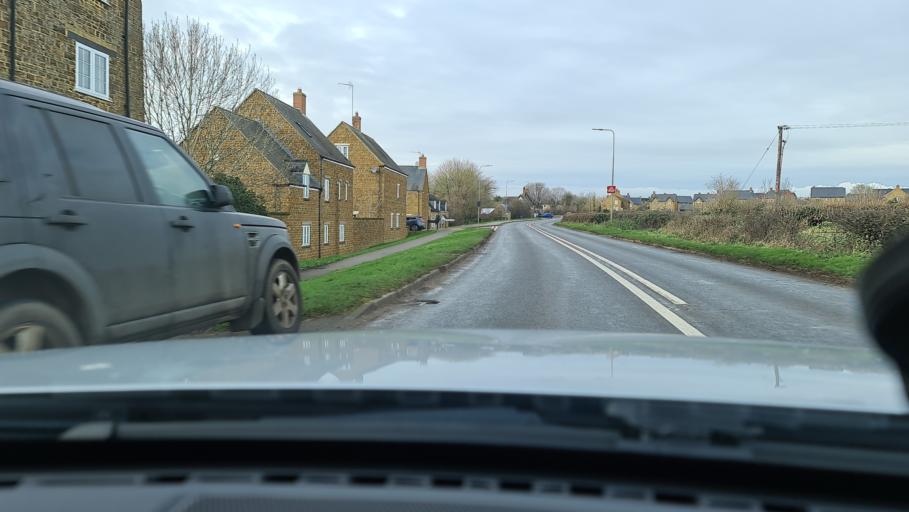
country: GB
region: England
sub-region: Oxfordshire
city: Adderbury
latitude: 52.0178
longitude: -1.3015
